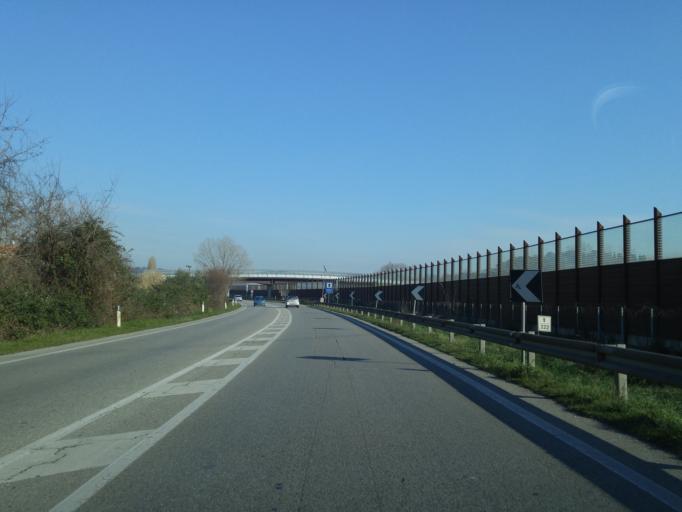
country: IT
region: Emilia-Romagna
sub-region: Provincia di Rimini
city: Cattolica
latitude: 43.9509
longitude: 12.7376
